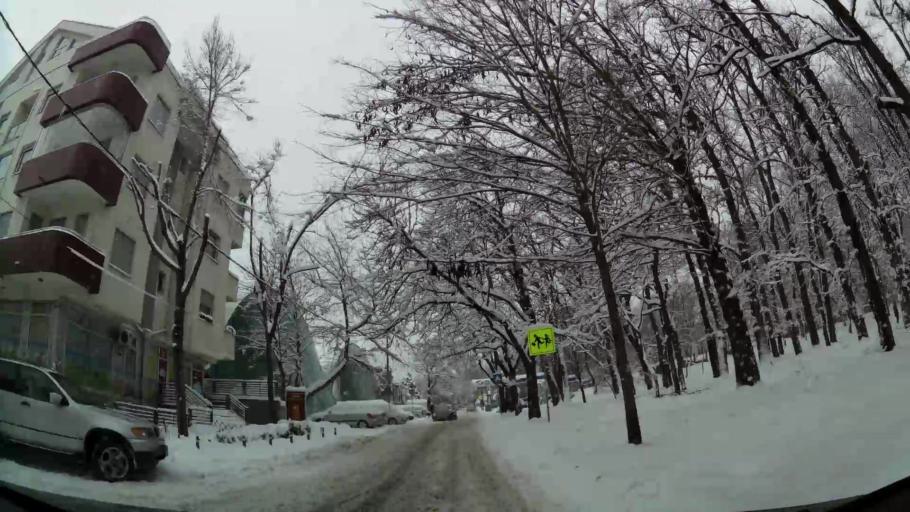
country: RS
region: Central Serbia
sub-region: Belgrade
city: Vracar
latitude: 44.7874
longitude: 20.4878
